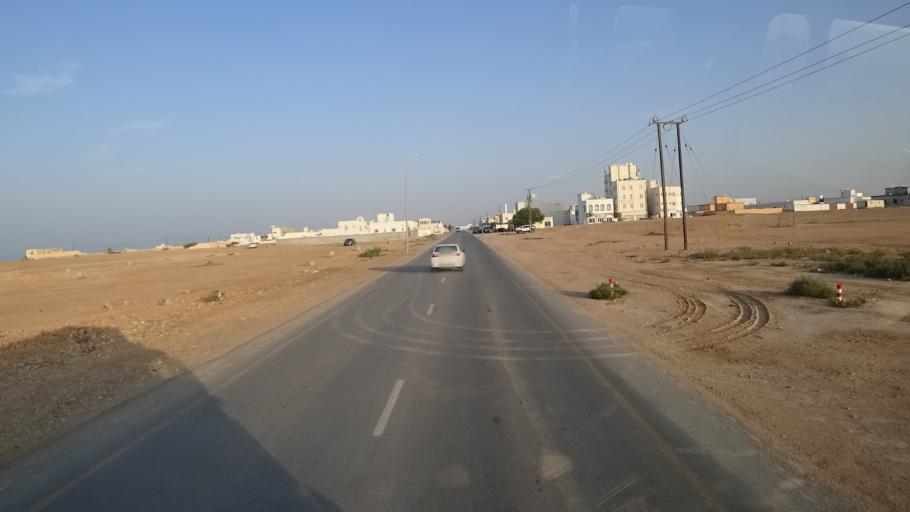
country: OM
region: Ash Sharqiyah
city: Sur
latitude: 22.6162
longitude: 59.4610
